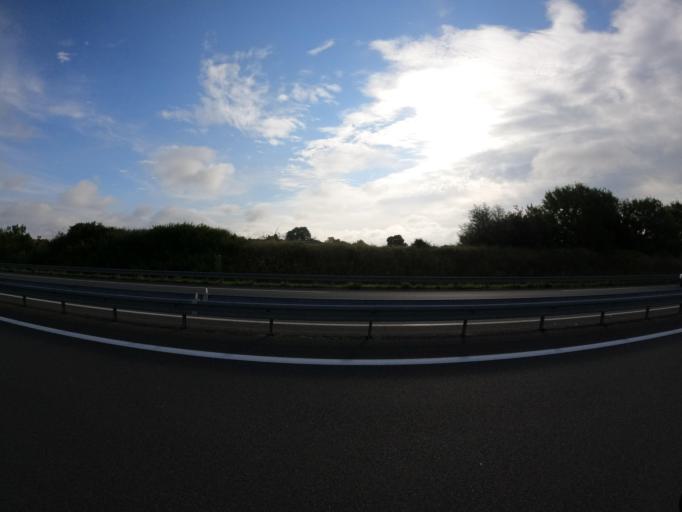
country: FR
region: Pays de la Loire
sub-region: Departement de Maine-et-Loire
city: Vivy
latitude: 47.3031
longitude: -0.0328
